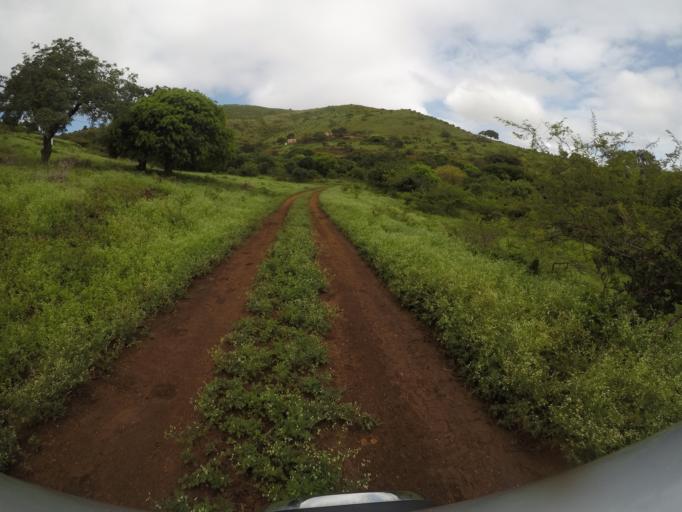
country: ZA
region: KwaZulu-Natal
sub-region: uThungulu District Municipality
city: Empangeni
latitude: -28.6331
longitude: 31.8748
